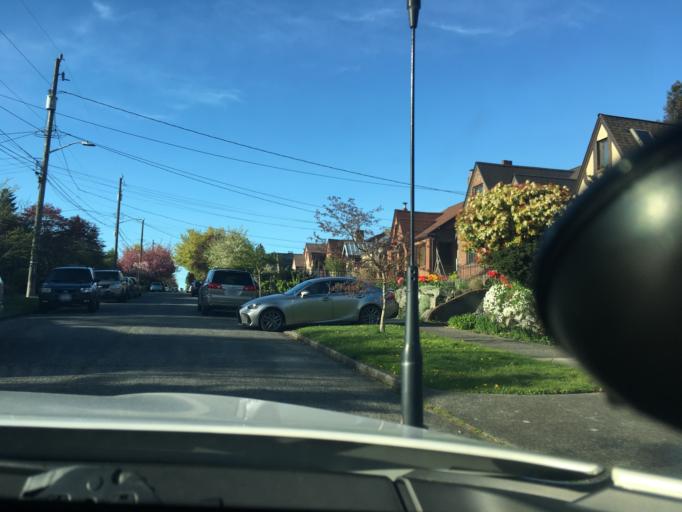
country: US
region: Washington
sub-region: King County
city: Shoreline
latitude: 47.6814
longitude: -122.3919
